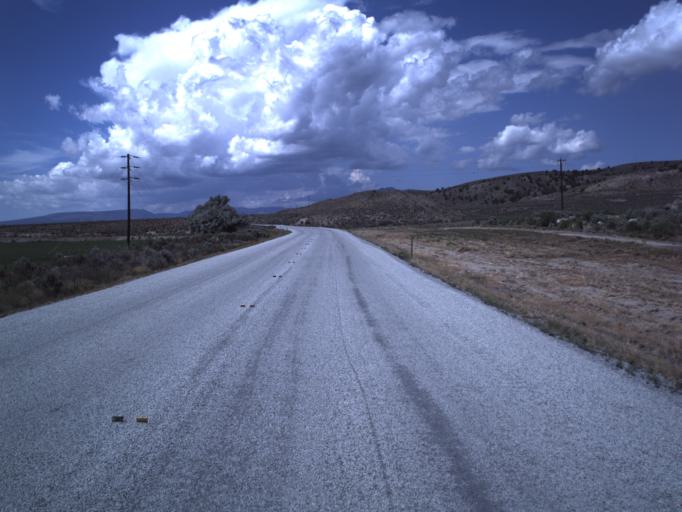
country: US
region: Utah
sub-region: Garfield County
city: Panguitch
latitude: 38.0228
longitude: -112.3619
